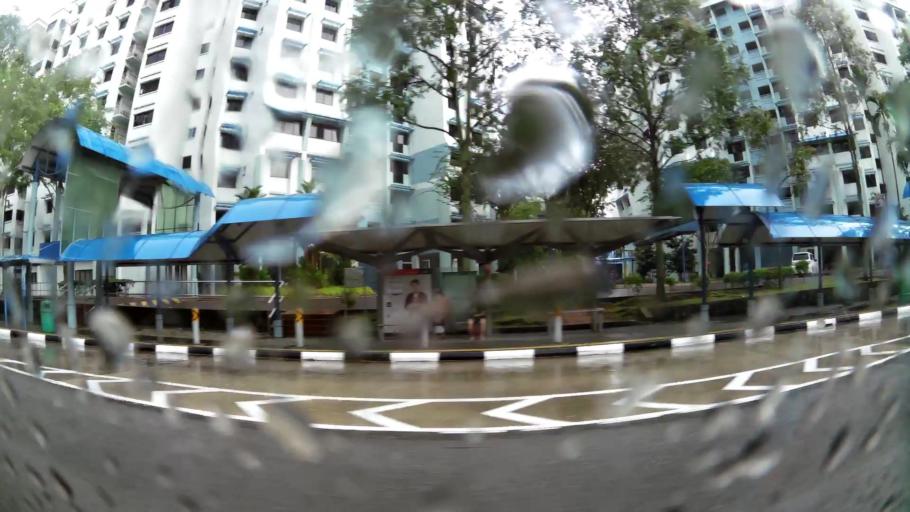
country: MY
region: Johor
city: Kampung Pasir Gudang Baru
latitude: 1.3873
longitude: 103.9018
